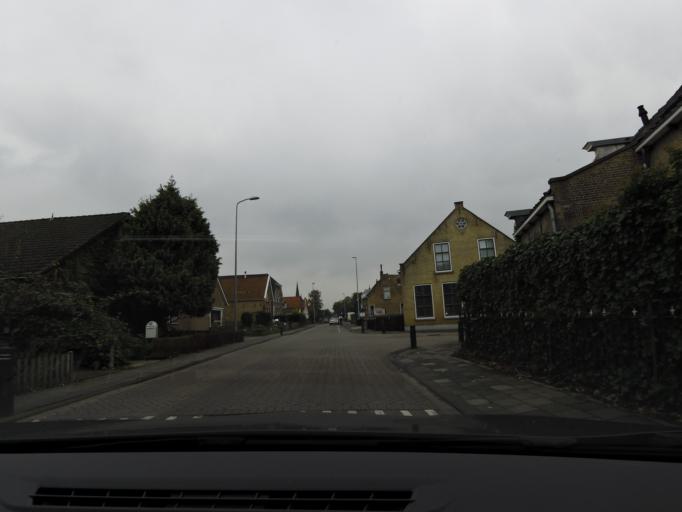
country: NL
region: South Holland
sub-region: Gemeente Goeree-Overflakkee
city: Middelharnis
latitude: 51.7599
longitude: 4.1550
